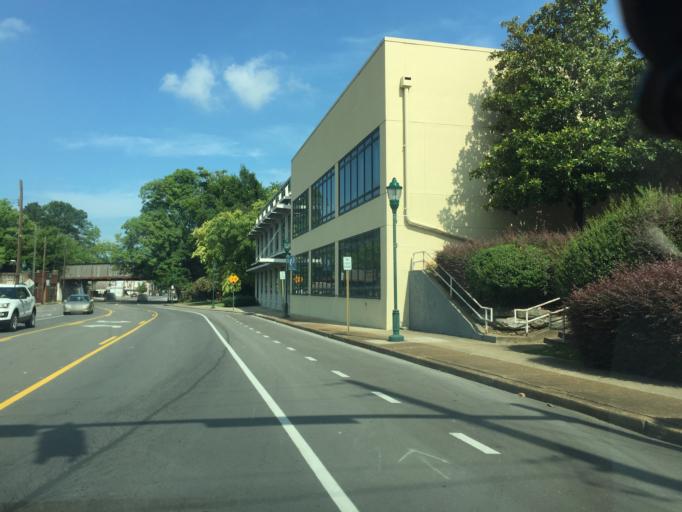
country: US
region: Tennessee
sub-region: Hamilton County
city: Chattanooga
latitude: 35.0424
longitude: -85.2989
